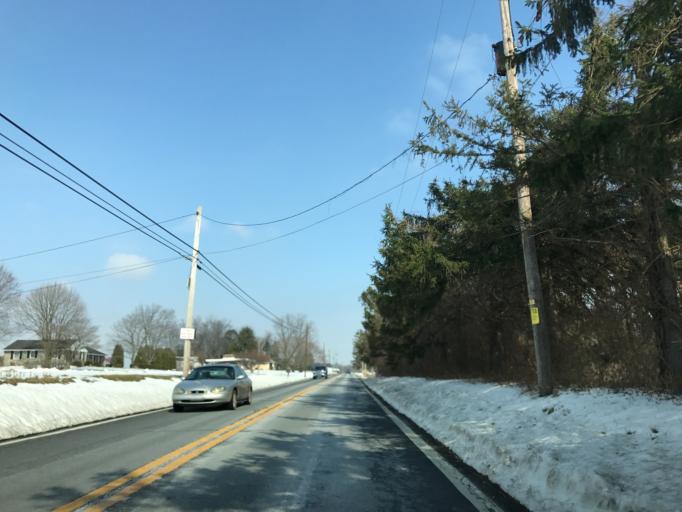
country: US
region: Pennsylvania
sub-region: York County
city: Susquehanna Trails
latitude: 39.7165
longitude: -76.3637
